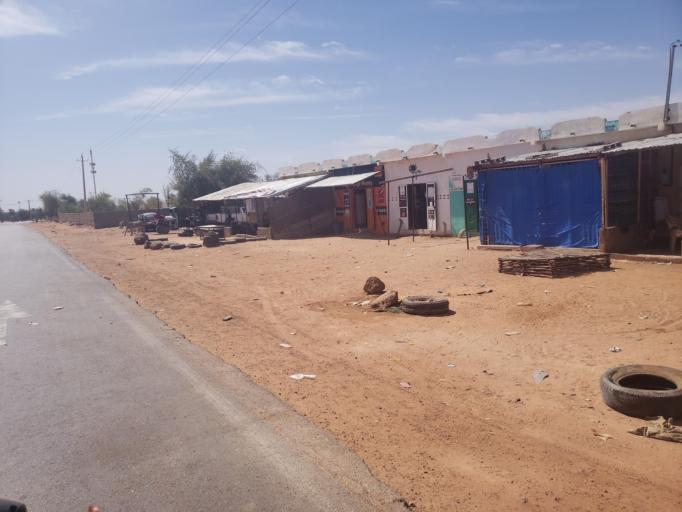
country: SN
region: Matam
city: Ranerou
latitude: 15.2978
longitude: -13.9570
